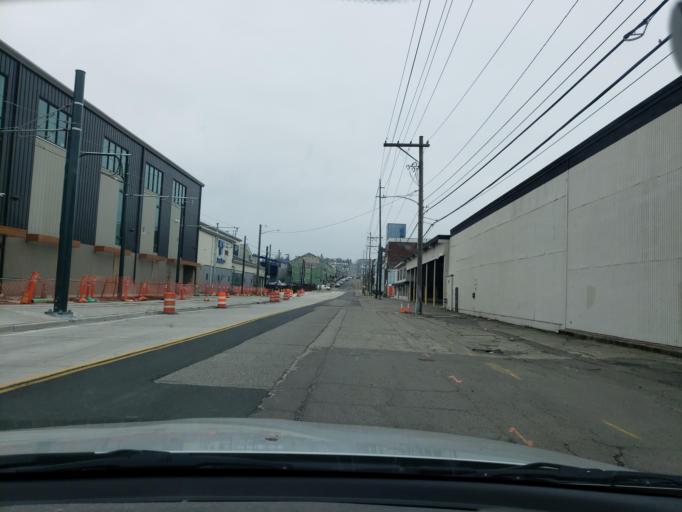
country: US
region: Washington
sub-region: Pierce County
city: Tacoma
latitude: 47.2405
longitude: -122.4216
